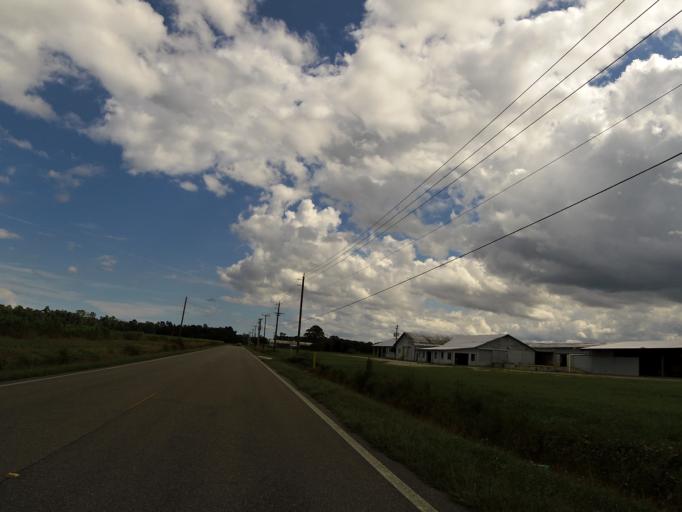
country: US
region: Florida
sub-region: Saint Johns County
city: Saint Augustine South
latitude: 29.8264
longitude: -81.4928
